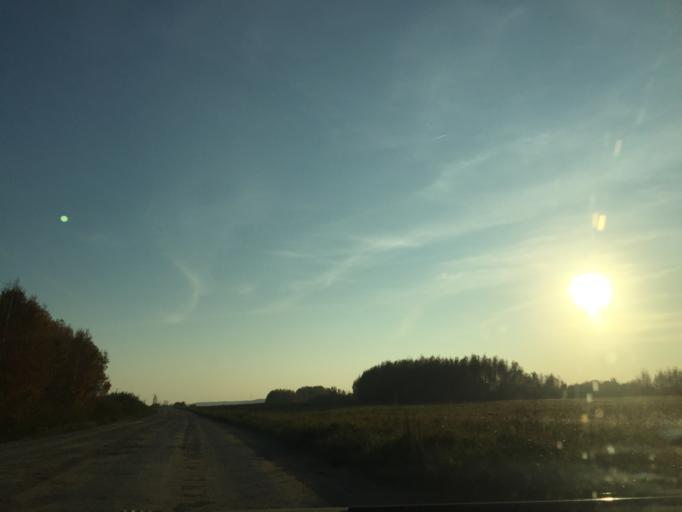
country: LV
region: Vainode
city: Vainode
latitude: 56.5385
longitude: 21.8355
